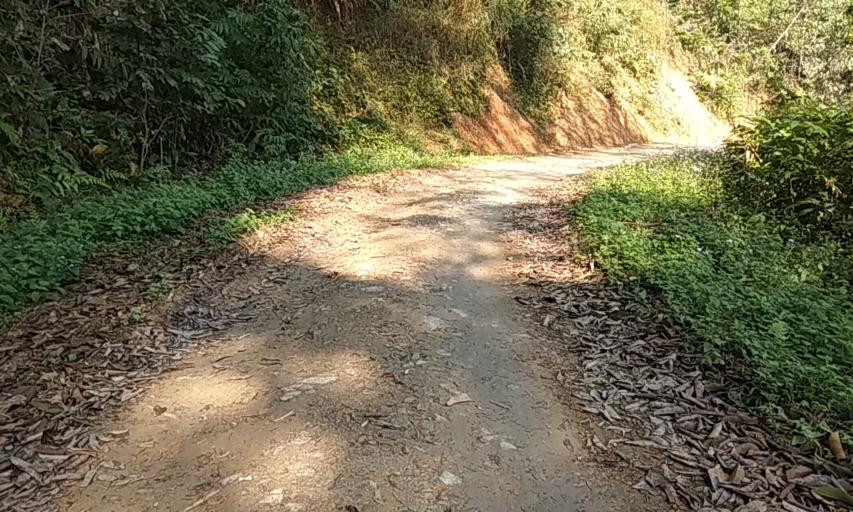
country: LA
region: Phongsali
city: Phongsali
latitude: 21.6975
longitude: 102.0646
